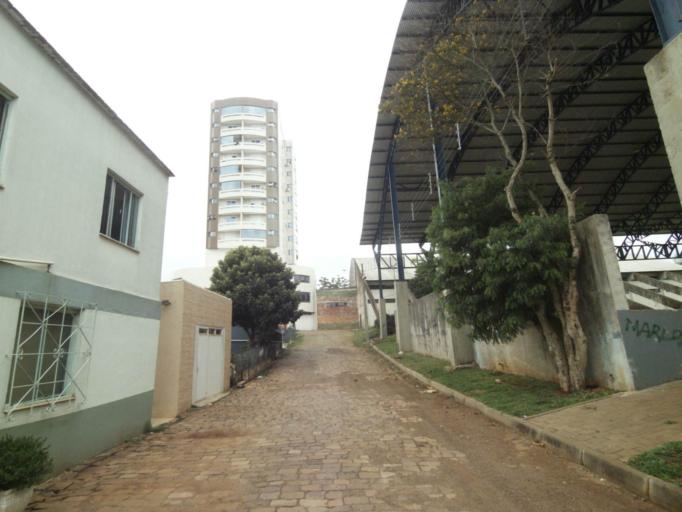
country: BR
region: Rio Grande do Sul
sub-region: Lagoa Vermelha
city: Lagoa Vermelha
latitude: -28.2140
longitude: -51.5201
